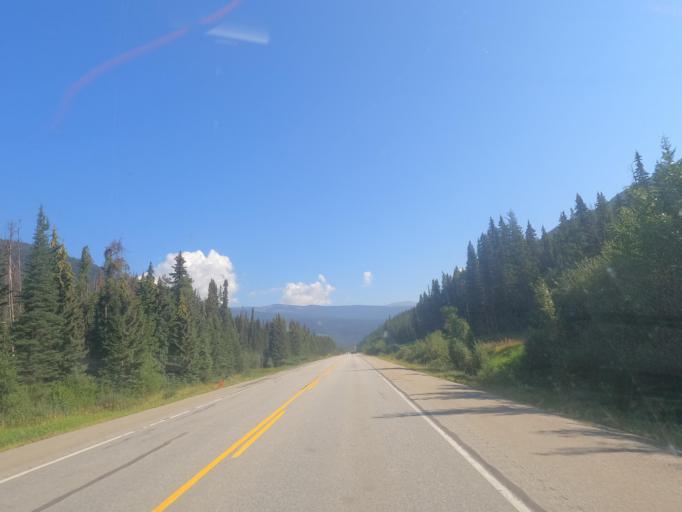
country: CA
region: Alberta
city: Jasper Park Lodge
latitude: 52.8699
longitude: -118.5049
